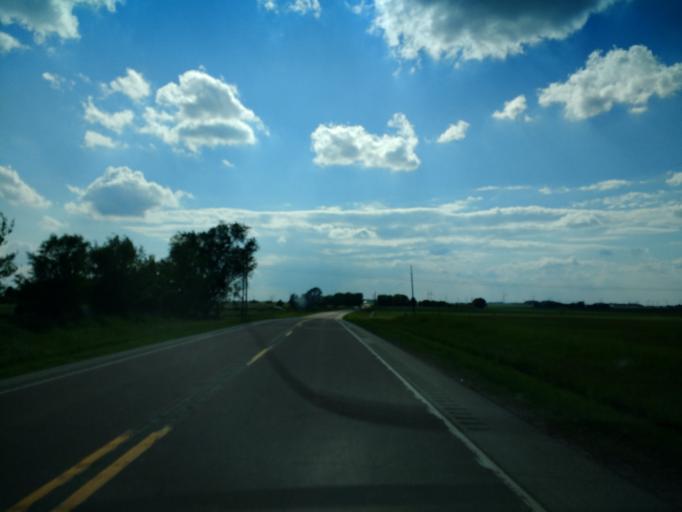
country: US
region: Iowa
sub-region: Clay County
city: Spencer
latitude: 43.1834
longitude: -95.2385
